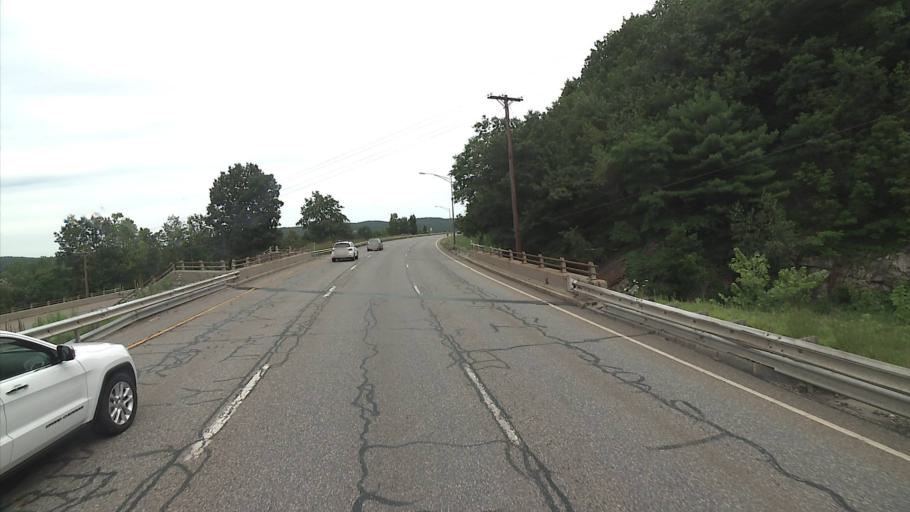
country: US
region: Connecticut
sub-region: Litchfield County
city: Torrington
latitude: 41.7979
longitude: -73.1125
